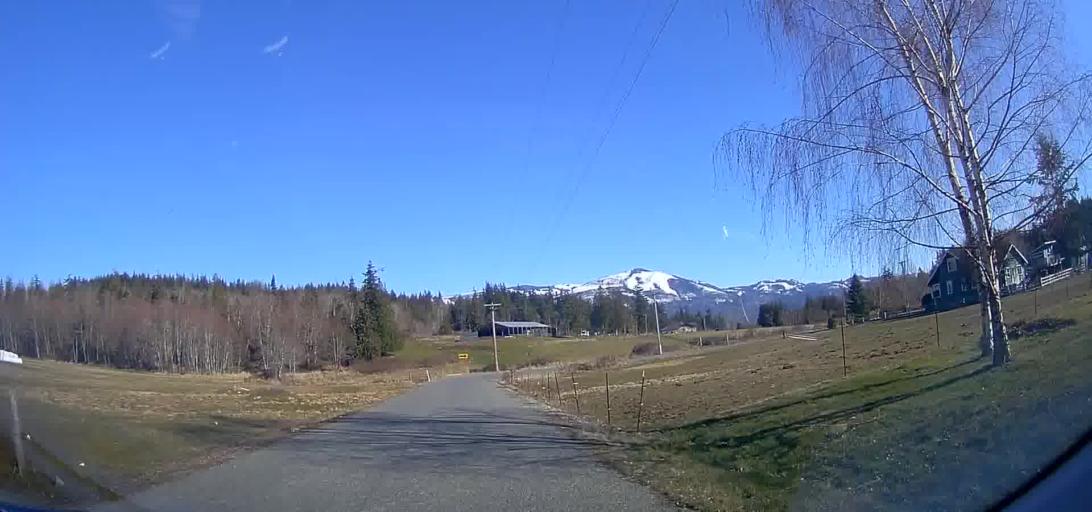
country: US
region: Washington
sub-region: Skagit County
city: Clear Lake
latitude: 48.4495
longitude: -122.2598
